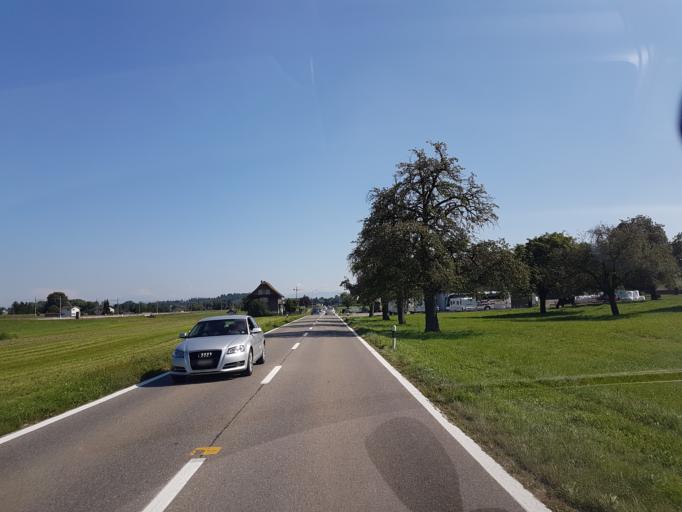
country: CH
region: Aargau
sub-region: Bezirk Muri
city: Muri
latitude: 47.2849
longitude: 8.3289
